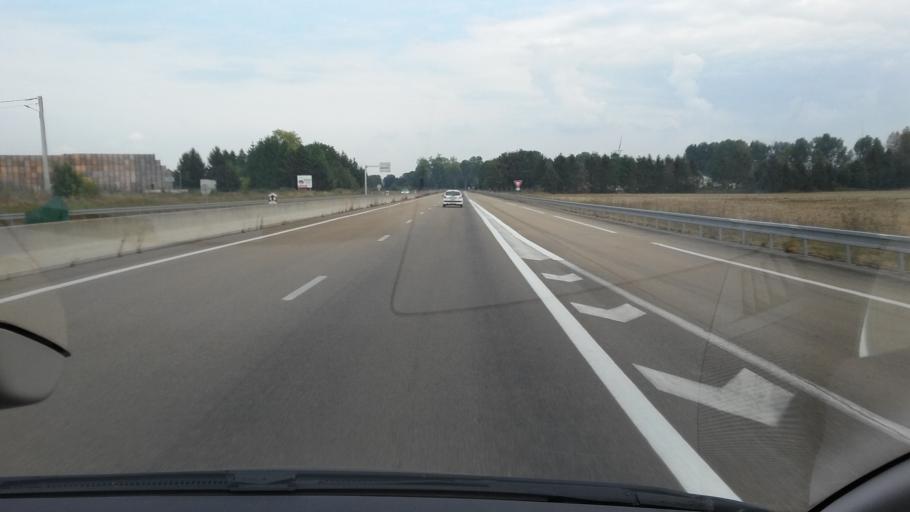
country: FR
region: Champagne-Ardenne
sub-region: Departement de la Marne
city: Fere-Champenoise
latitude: 48.7449
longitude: 3.9694
